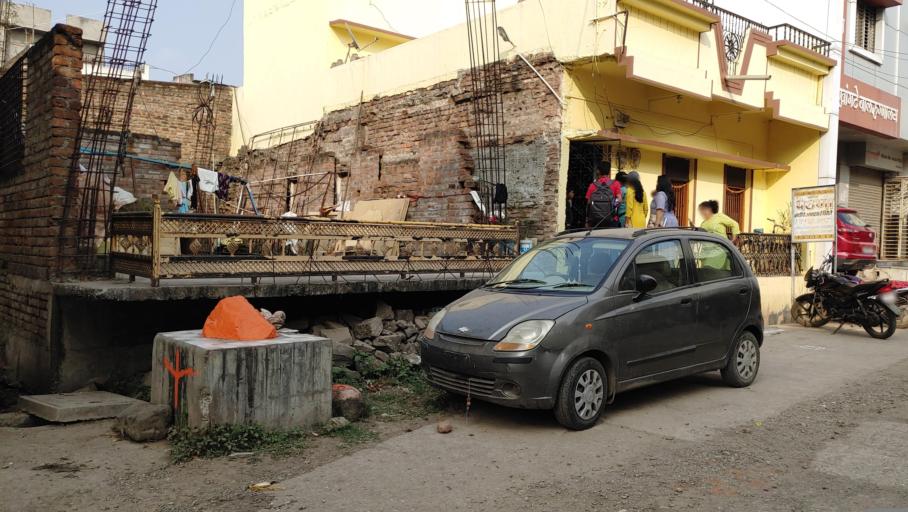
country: IN
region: Maharashtra
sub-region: Nashik Division
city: Yeola
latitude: 20.0390
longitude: 74.4890
